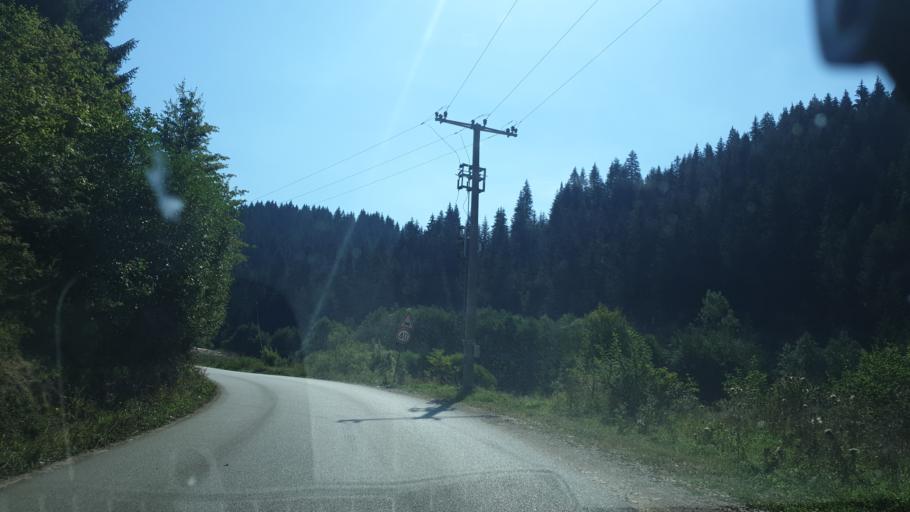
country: RS
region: Central Serbia
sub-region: Zlatiborski Okrug
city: Nova Varos
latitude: 43.4502
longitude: 19.8451
